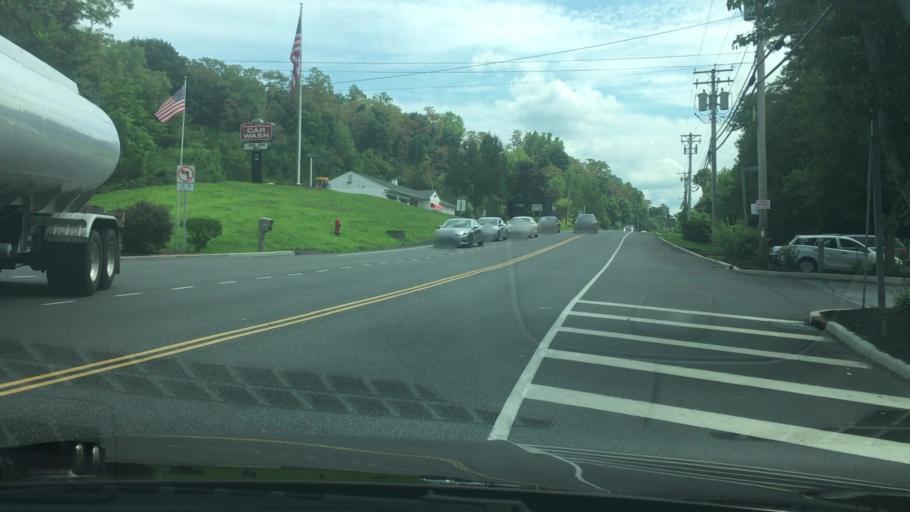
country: US
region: New York
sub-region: Dutchess County
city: Red Oaks Mill
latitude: 41.6592
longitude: -73.8483
